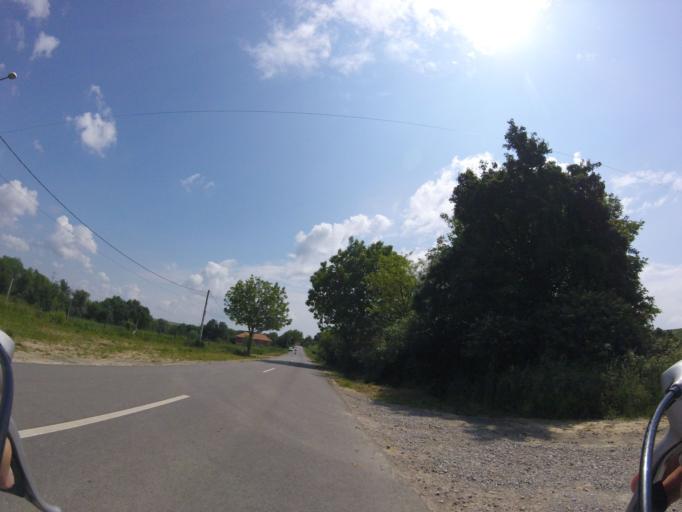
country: HU
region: Baranya
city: Kozarmisleny
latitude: 46.0843
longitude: 18.3097
